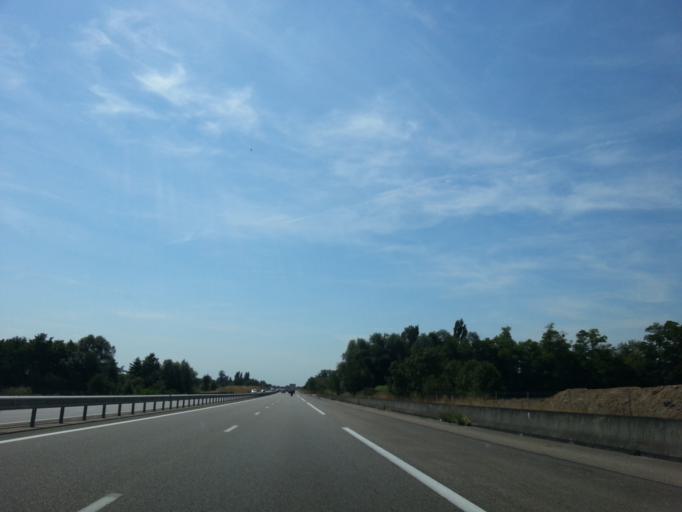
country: FR
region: Alsace
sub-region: Departement du Bas-Rhin
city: Stotzheim
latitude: 48.3868
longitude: 7.4774
